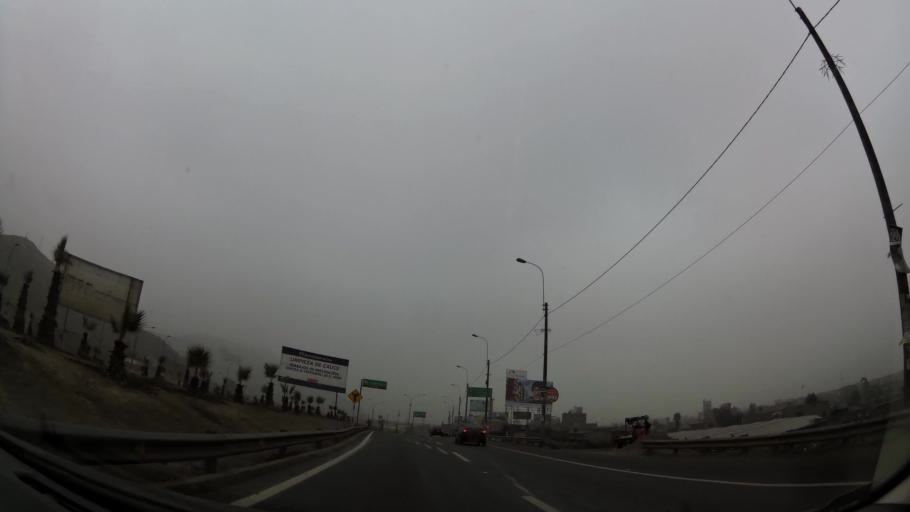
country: PE
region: Lima
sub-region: Lima
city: Santa Maria
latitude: -12.0144
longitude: -76.9032
